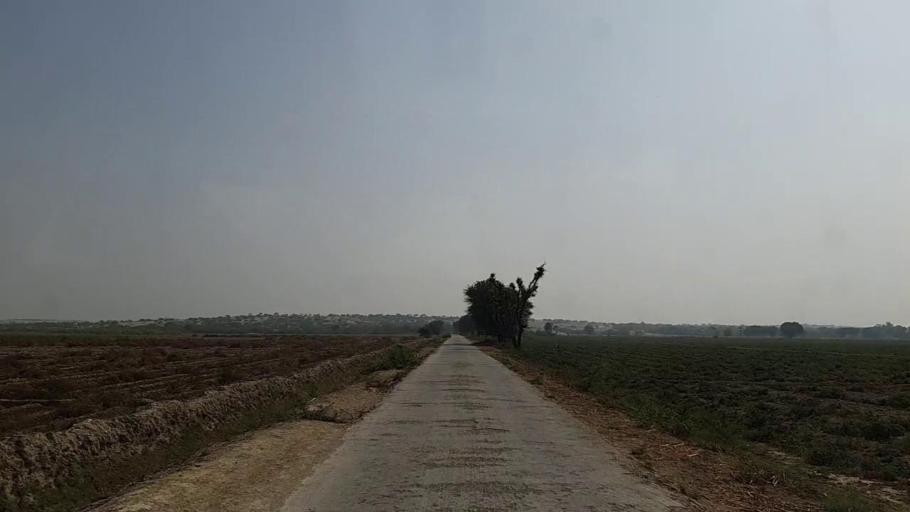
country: PK
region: Sindh
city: Naukot
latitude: 24.7518
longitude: 69.3472
